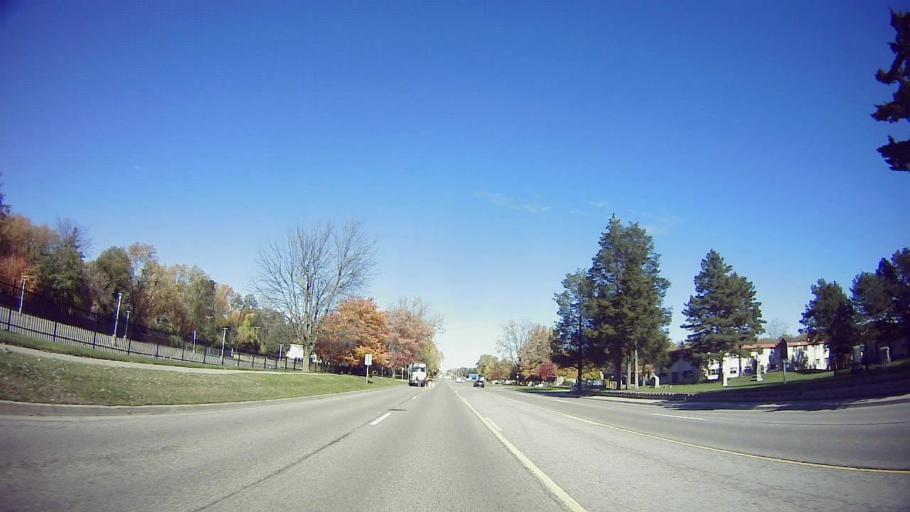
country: US
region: Michigan
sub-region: Oakland County
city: Southfield
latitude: 42.4748
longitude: -83.2609
